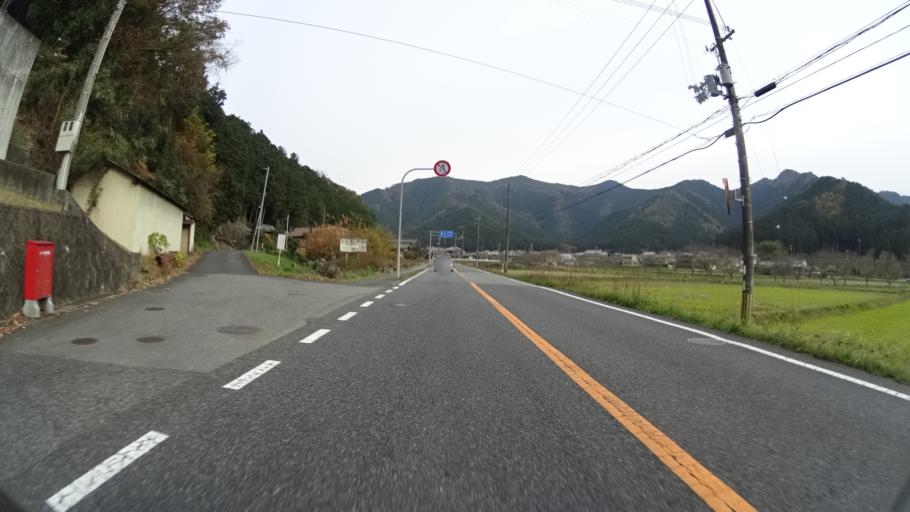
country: JP
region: Hyogo
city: Sasayama
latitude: 35.1176
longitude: 135.0912
